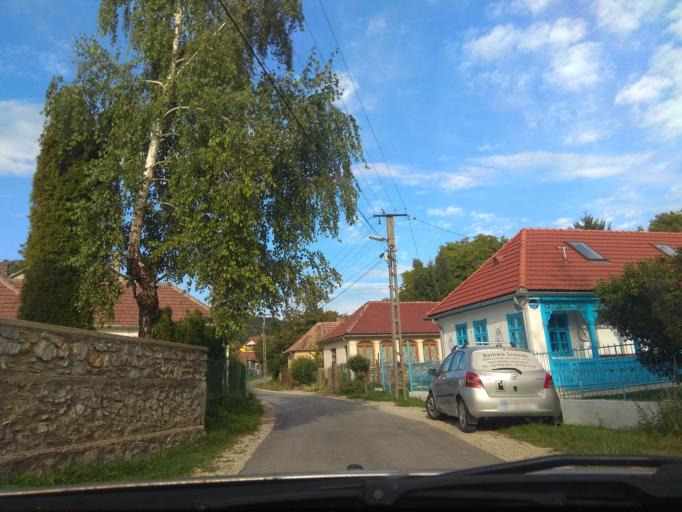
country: HU
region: Borsod-Abauj-Zemplen
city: Saly
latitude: 48.0684
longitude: 20.6329
